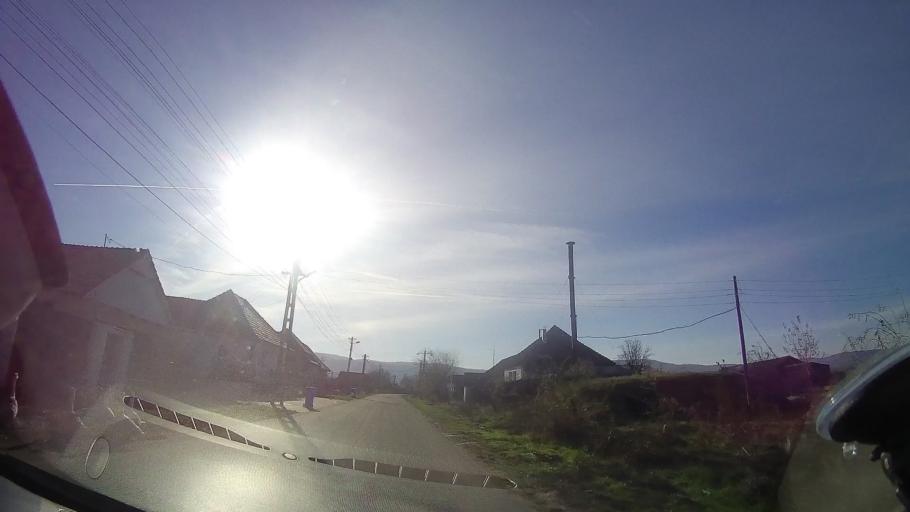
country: RO
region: Bihor
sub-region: Comuna Magesti
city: Magesti
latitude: 47.0198
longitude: 22.4686
